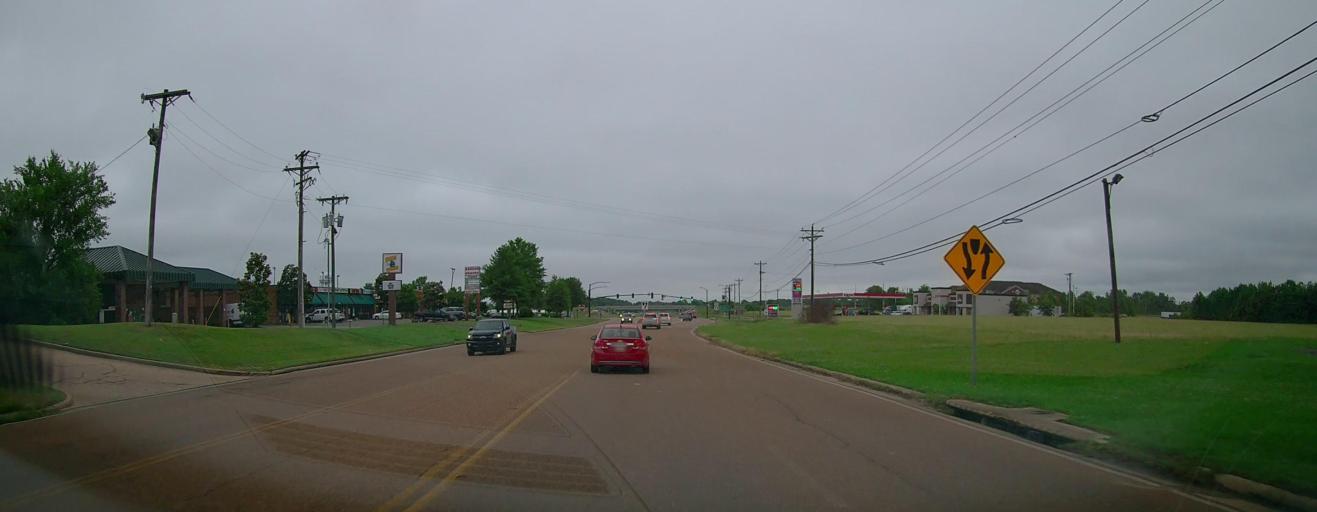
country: US
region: Mississippi
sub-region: De Soto County
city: Olive Branch
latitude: 34.9317
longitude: -89.7949
